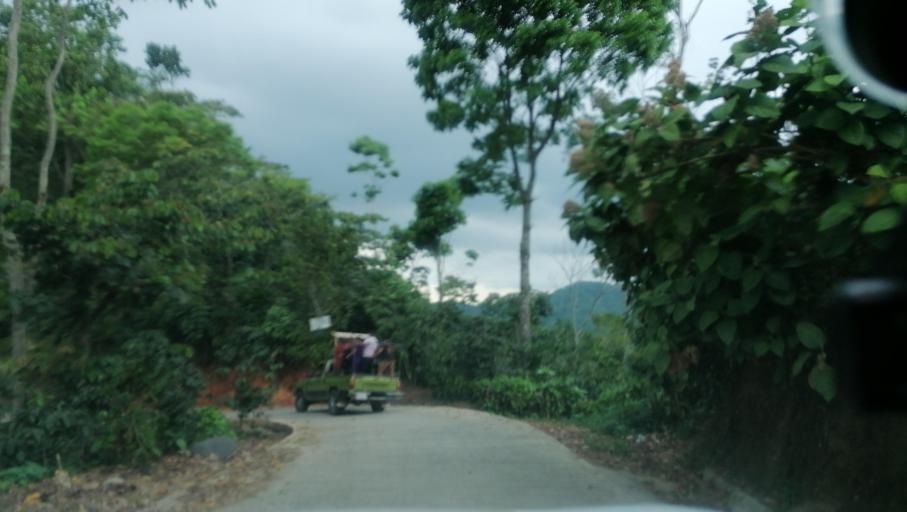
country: MX
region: Chiapas
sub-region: Cacahoatan
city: Benito Juarez
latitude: 15.0720
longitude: -92.1630
